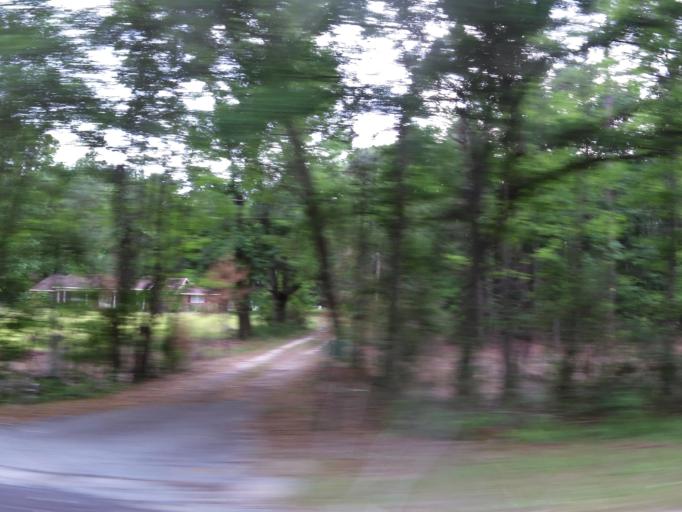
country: US
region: South Carolina
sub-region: Jasper County
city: Hardeeville
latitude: 32.3295
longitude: -81.0903
